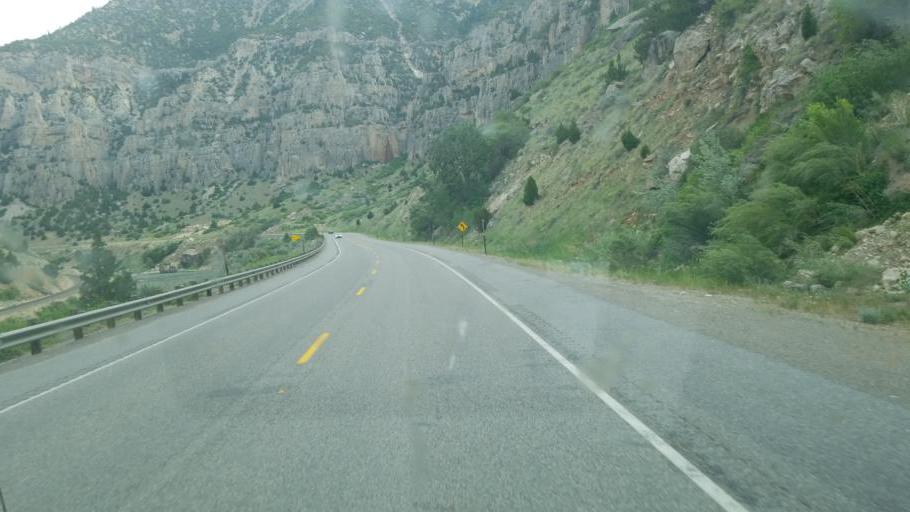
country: US
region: Wyoming
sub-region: Hot Springs County
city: Thermopolis
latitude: 43.5216
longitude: -108.1776
